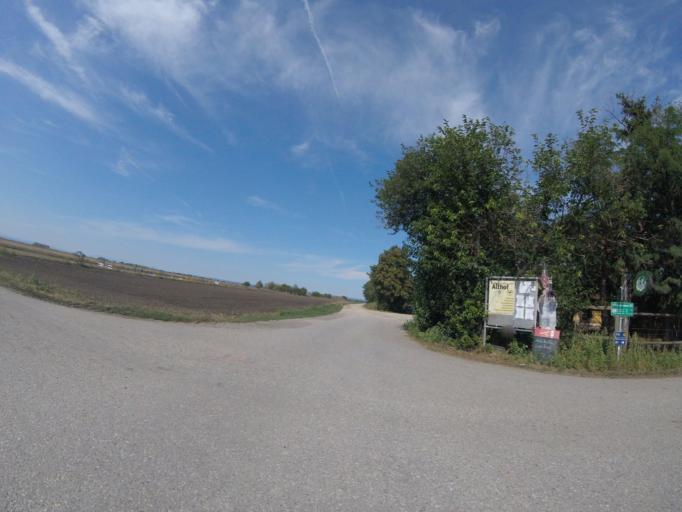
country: AT
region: Burgenland
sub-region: Politischer Bezirk Neusiedl am See
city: Frauenkirchen
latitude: 47.8248
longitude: 16.8919
